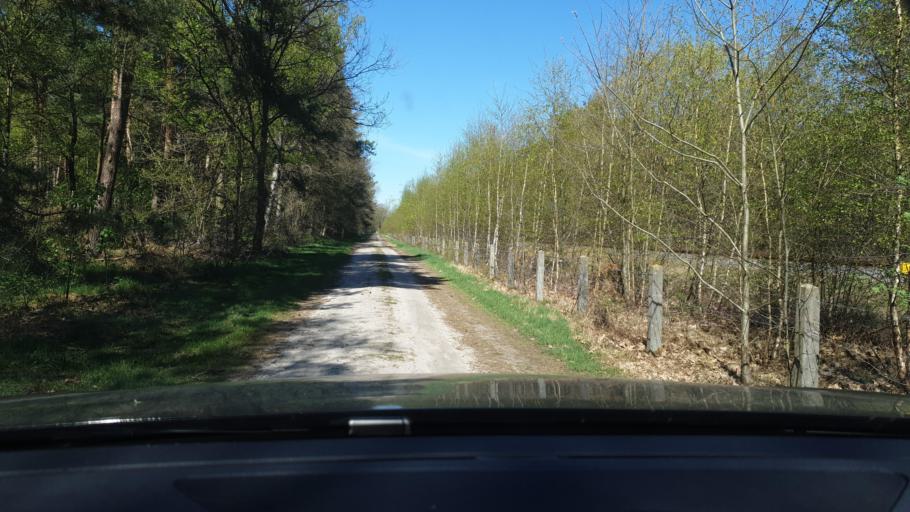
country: NL
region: Limburg
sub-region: Gemeente Venlo
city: Arcen
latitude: 51.4481
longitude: 6.1223
